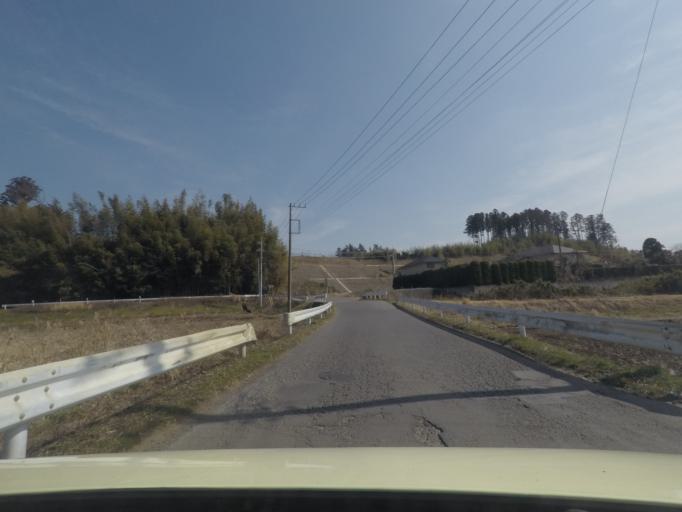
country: JP
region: Ibaraki
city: Ishioka
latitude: 36.1942
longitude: 140.3415
